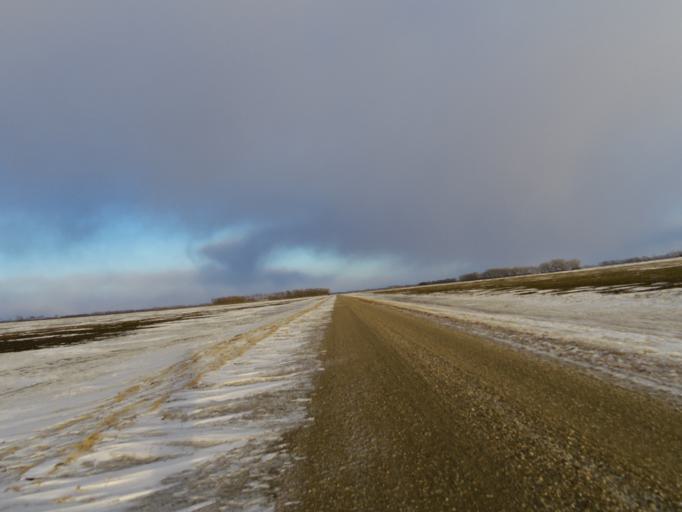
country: US
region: North Dakota
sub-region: Walsh County
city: Grafton
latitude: 48.3976
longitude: -97.2219
